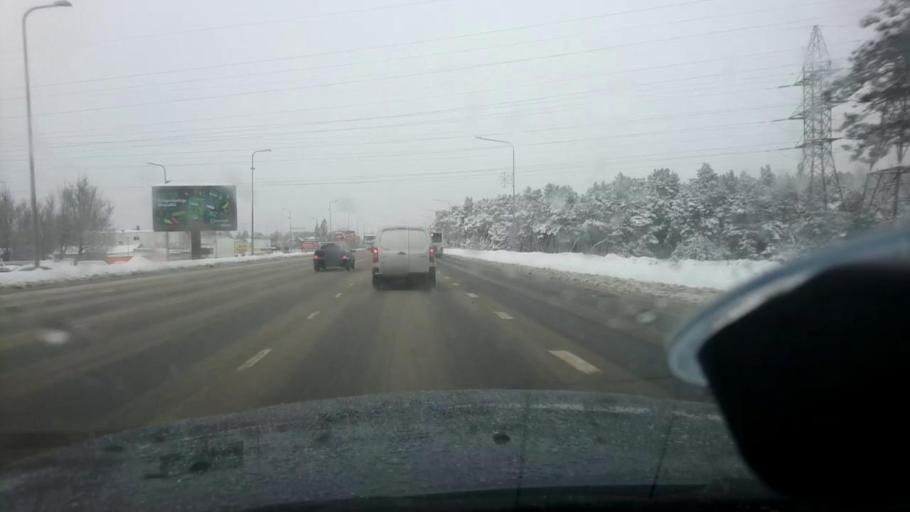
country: EE
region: Harju
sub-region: Tallinna linn
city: Tallinn
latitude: 59.3958
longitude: 24.7257
